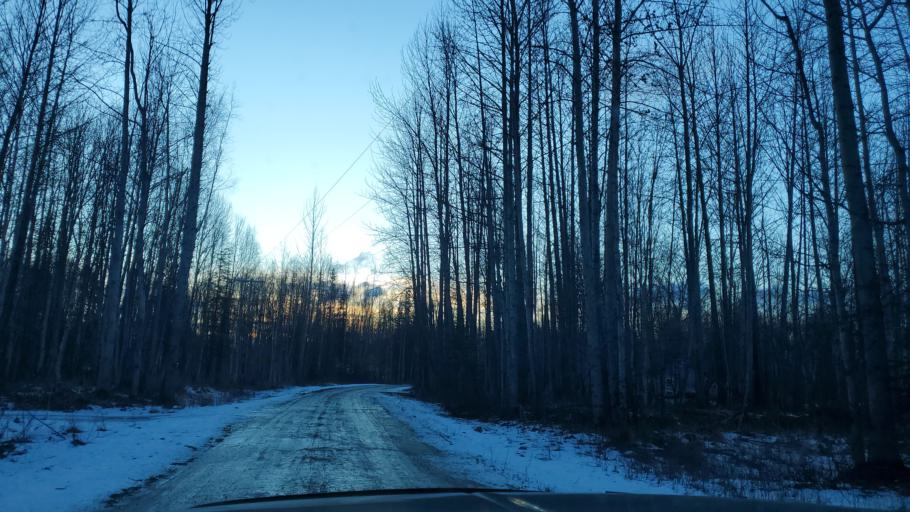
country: US
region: Alaska
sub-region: Matanuska-Susitna Borough
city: Lakes
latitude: 61.6667
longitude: -149.3326
